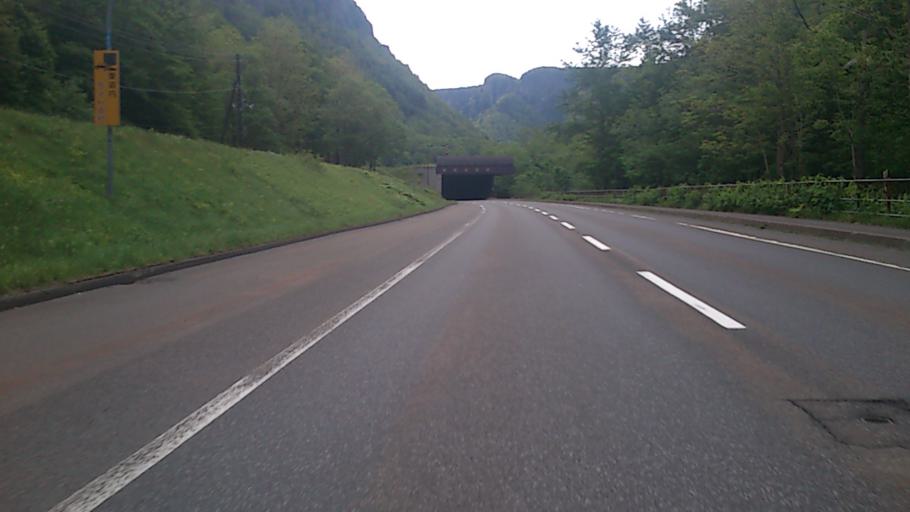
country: JP
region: Hokkaido
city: Kamikawa
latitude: 43.7395
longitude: 142.9374
